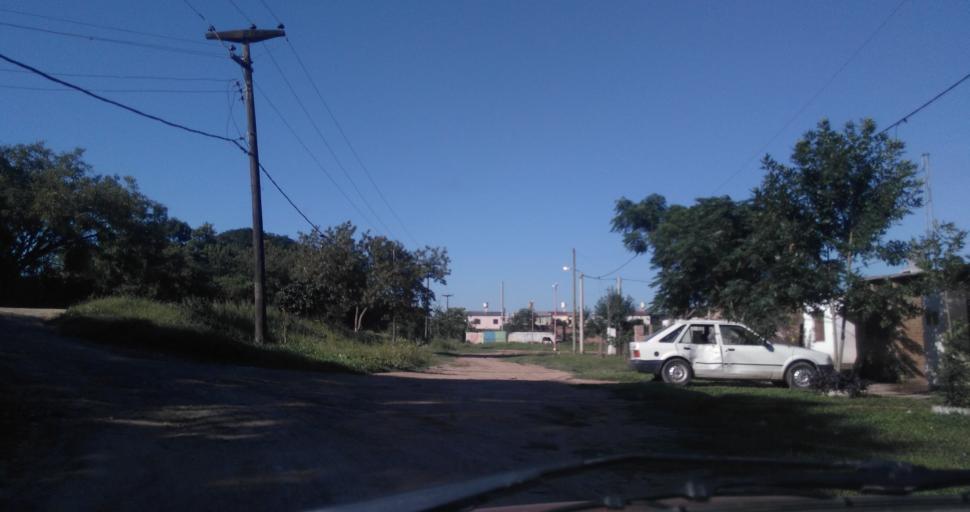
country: AR
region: Chaco
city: Resistencia
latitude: -27.4404
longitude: -58.9605
